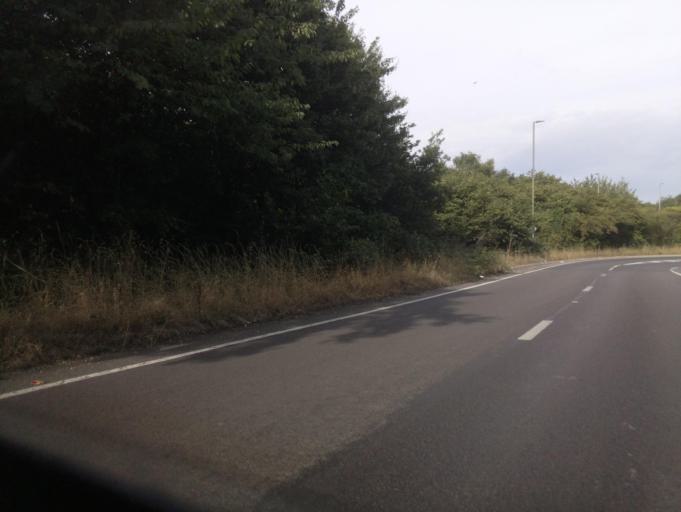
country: GB
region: England
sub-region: Surrey
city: Seale
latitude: 51.2280
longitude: -0.7406
